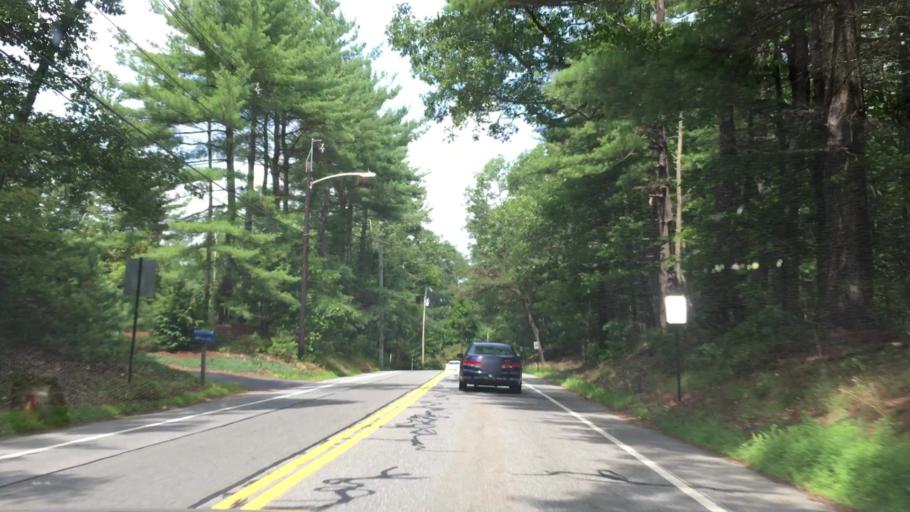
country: US
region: Massachusetts
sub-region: Middlesex County
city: Concord
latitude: 42.4458
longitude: -71.3411
